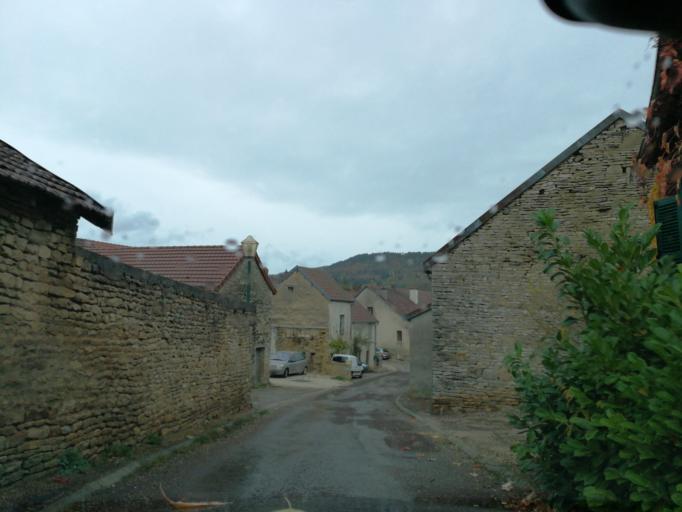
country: FR
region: Bourgogne
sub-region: Departement de la Cote-d'Or
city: Fleurey-sur-Ouche
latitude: 47.3223
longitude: 4.7920
